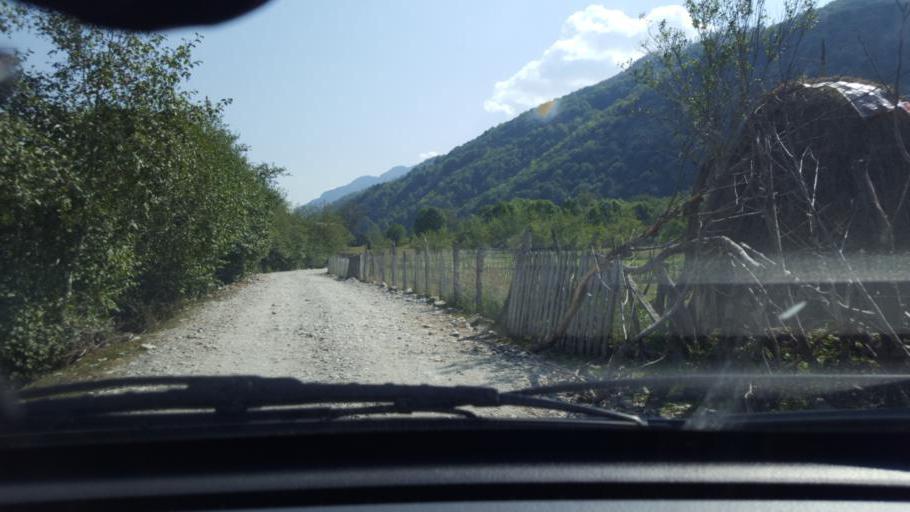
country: ME
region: Andrijevica
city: Andrijevica
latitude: 42.5911
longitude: 19.6874
